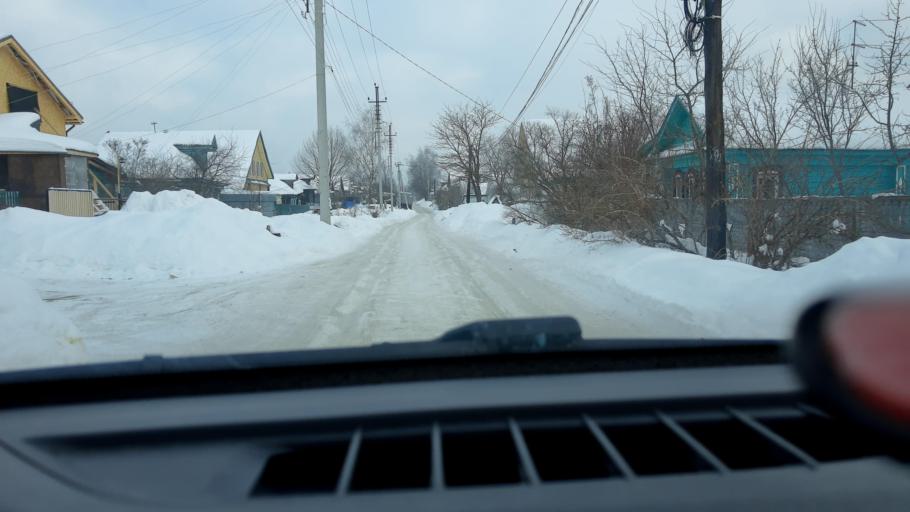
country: RU
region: Nizjnij Novgorod
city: Gorbatovka
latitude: 56.2603
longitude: 43.7364
